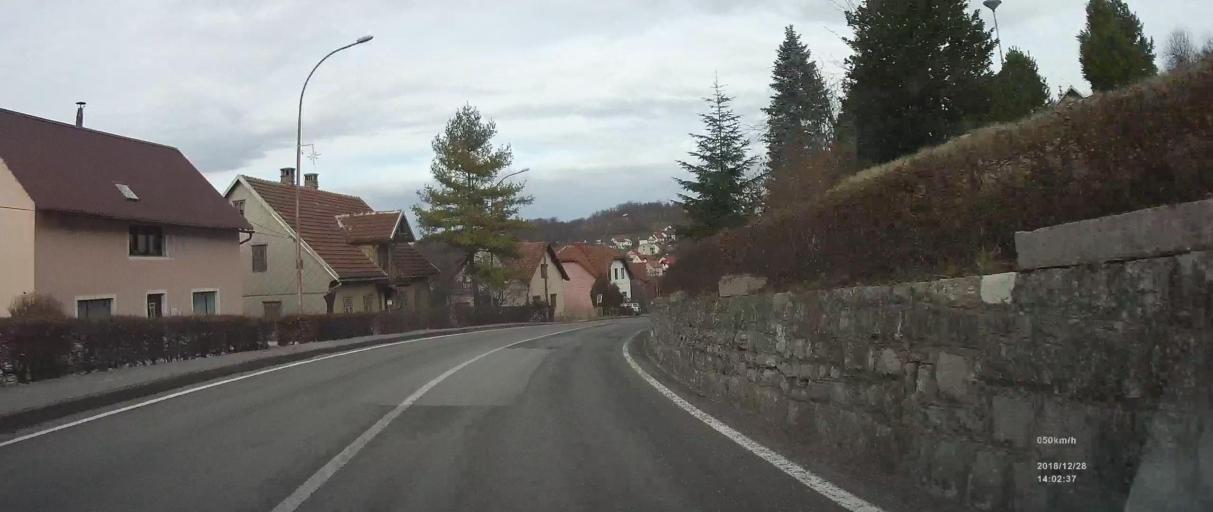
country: SI
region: Kostel
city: Kostel
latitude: 45.4305
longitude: 14.9041
